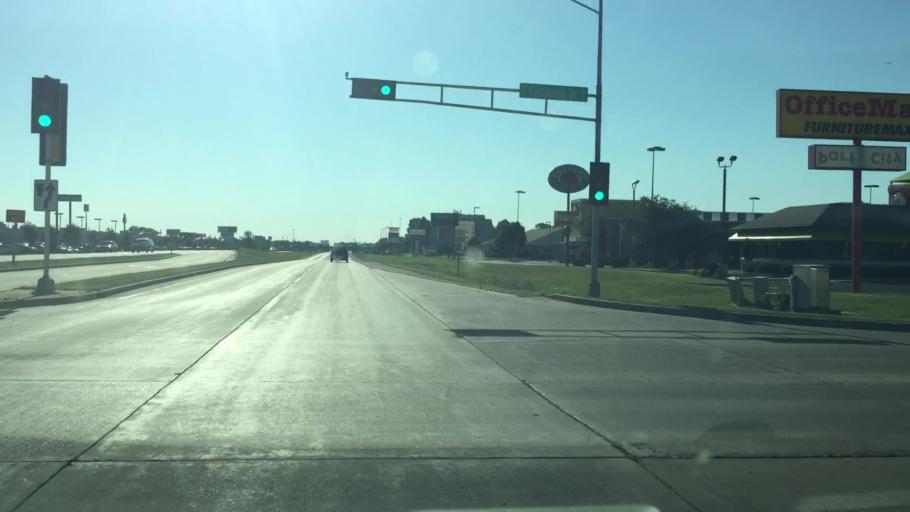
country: US
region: Wisconsin
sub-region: Outagamie County
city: Appleton
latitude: 44.2619
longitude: -88.4760
